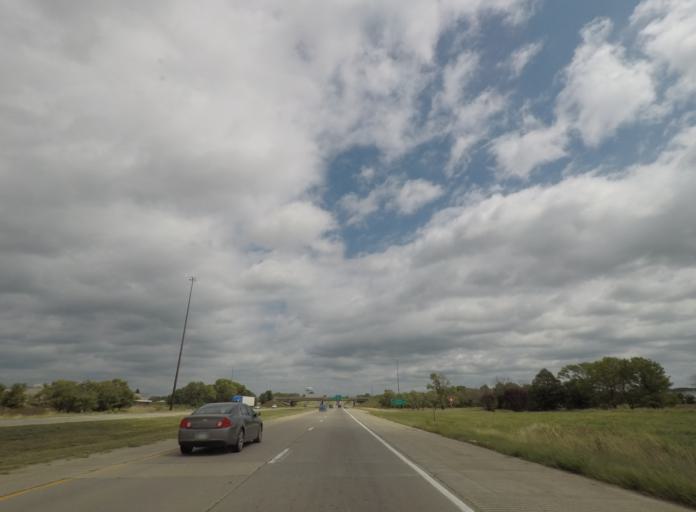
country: US
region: Iowa
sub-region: Linn County
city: Cedar Rapids
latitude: 41.9268
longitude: -91.6610
